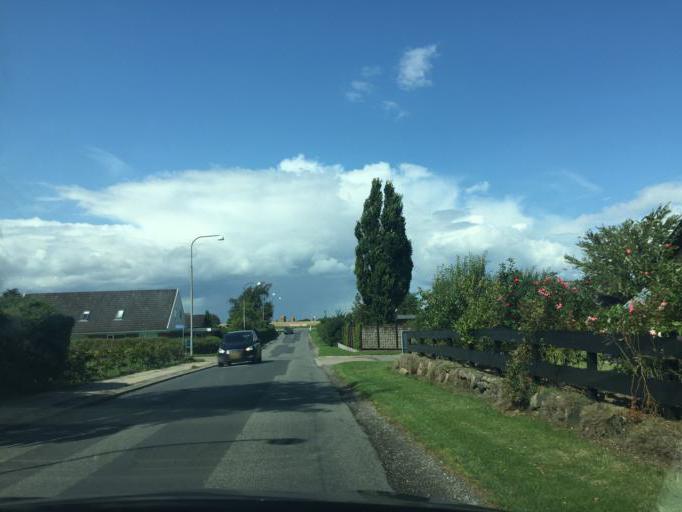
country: DK
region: South Denmark
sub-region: Faaborg-Midtfyn Kommune
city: Arslev
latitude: 55.3121
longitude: 10.4870
